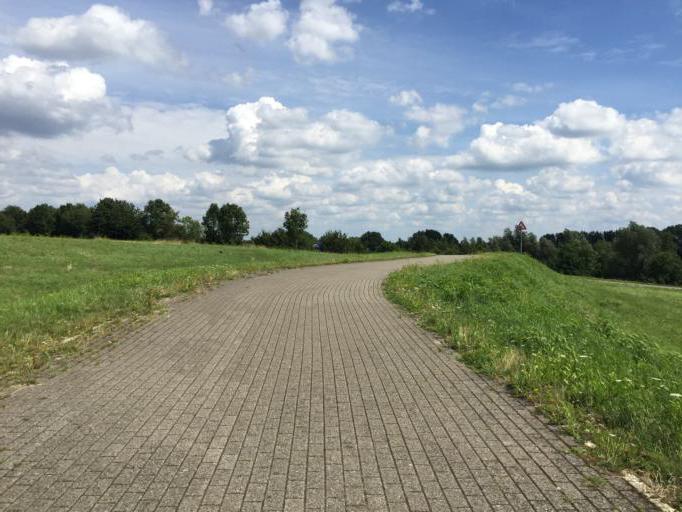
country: NL
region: Utrecht
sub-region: Gemeente Nieuwegein
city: Nieuwegein
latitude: 52.0381
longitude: 5.0588
